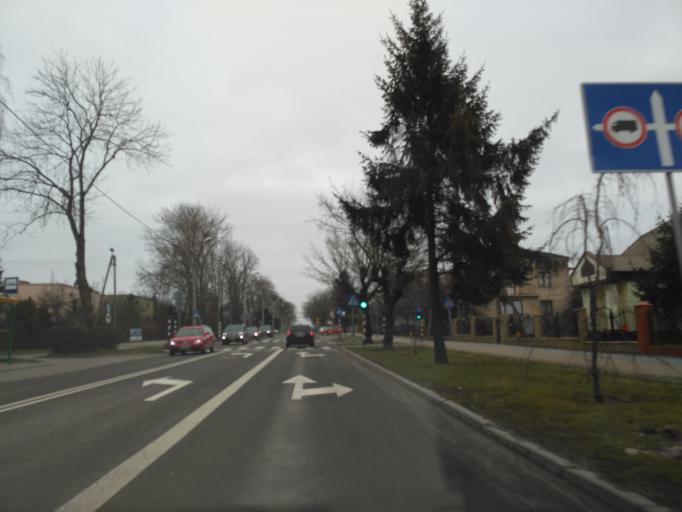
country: PL
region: Lublin Voivodeship
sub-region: Chelm
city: Chelm
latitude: 51.1257
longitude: 23.4933
